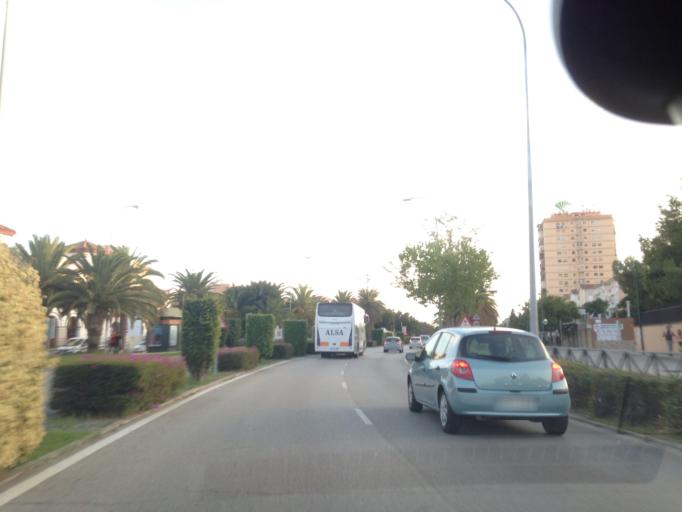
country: ES
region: Andalusia
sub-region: Provincia de Malaga
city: Malaga
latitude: 36.7469
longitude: -4.4227
